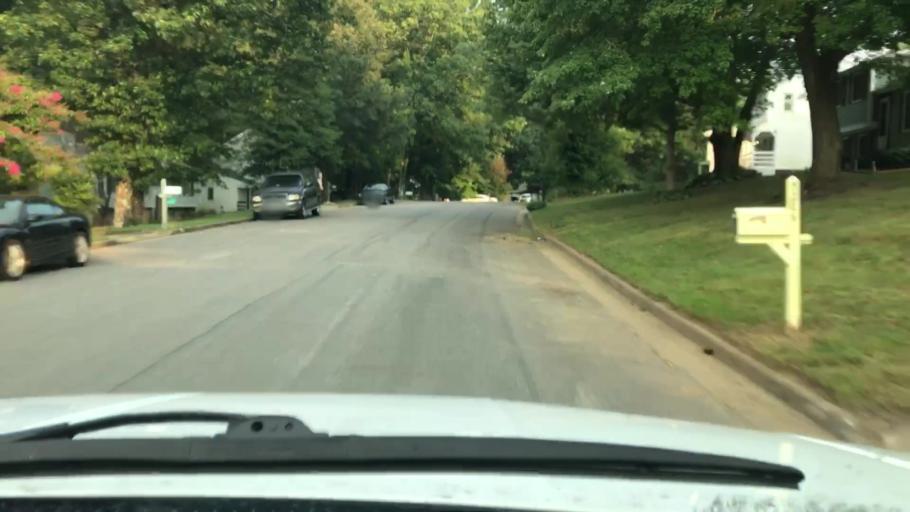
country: US
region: Virginia
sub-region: Chesterfield County
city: Chesterfield
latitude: 37.4418
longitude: -77.5168
